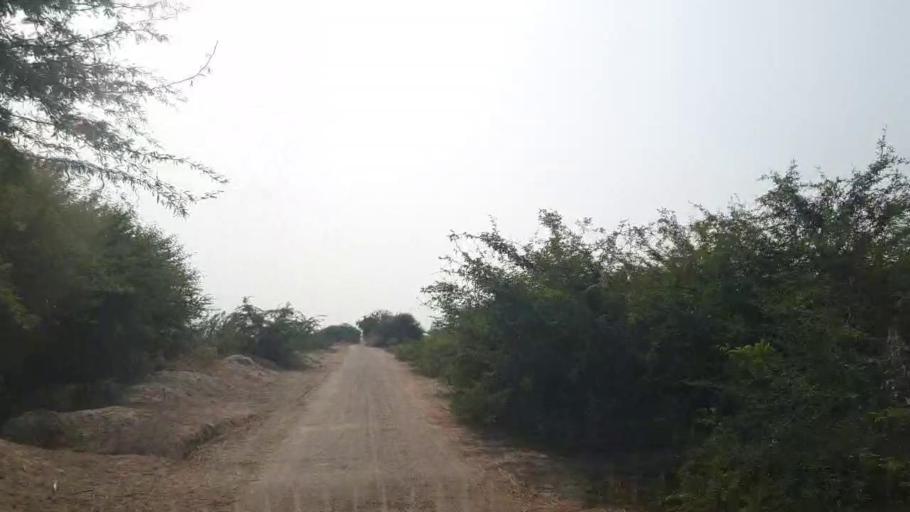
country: PK
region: Sindh
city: Badin
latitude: 24.7332
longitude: 68.7347
